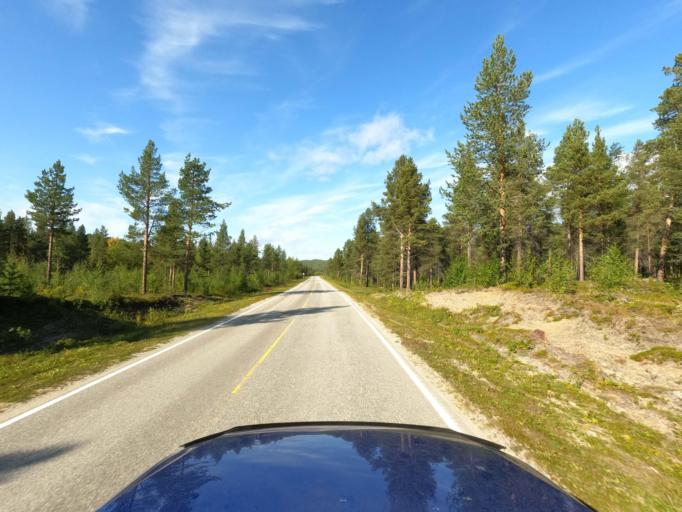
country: NO
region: Finnmark Fylke
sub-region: Porsanger
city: Lakselv
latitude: 69.8218
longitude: 25.1554
